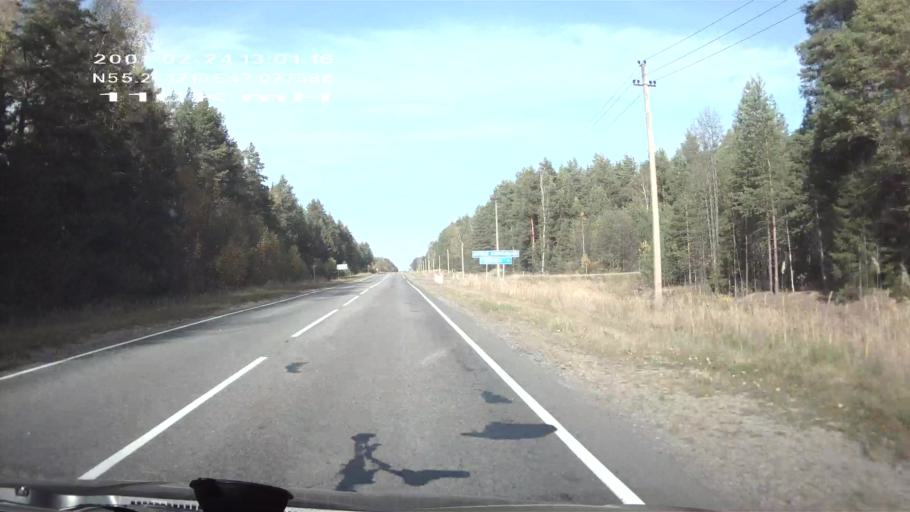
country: RU
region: Chuvashia
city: Buinsk
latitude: 55.2010
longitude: 47.0774
